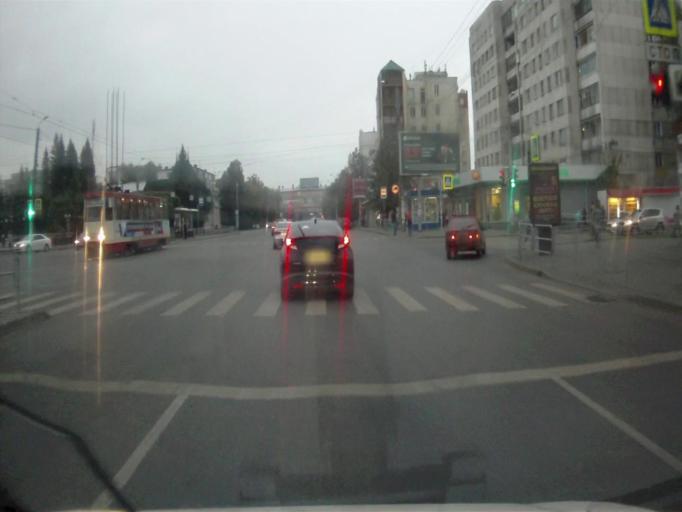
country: RU
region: Chelyabinsk
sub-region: Gorod Chelyabinsk
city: Chelyabinsk
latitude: 55.1792
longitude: 61.3995
